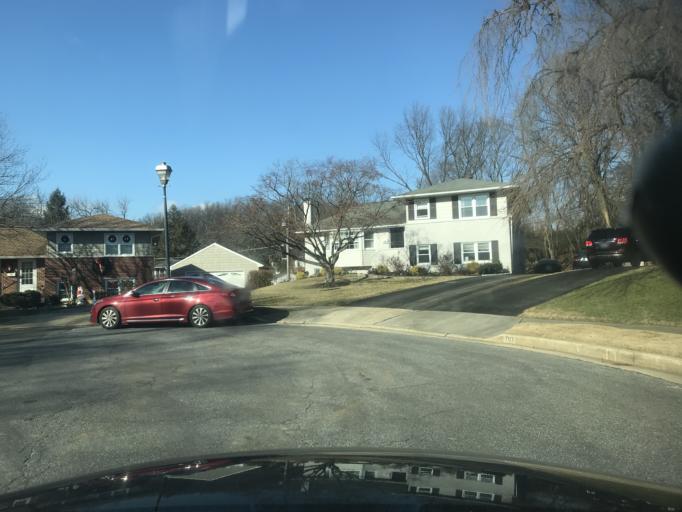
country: US
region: Maryland
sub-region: Baltimore County
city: Hampton
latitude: 39.4046
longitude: -76.5836
